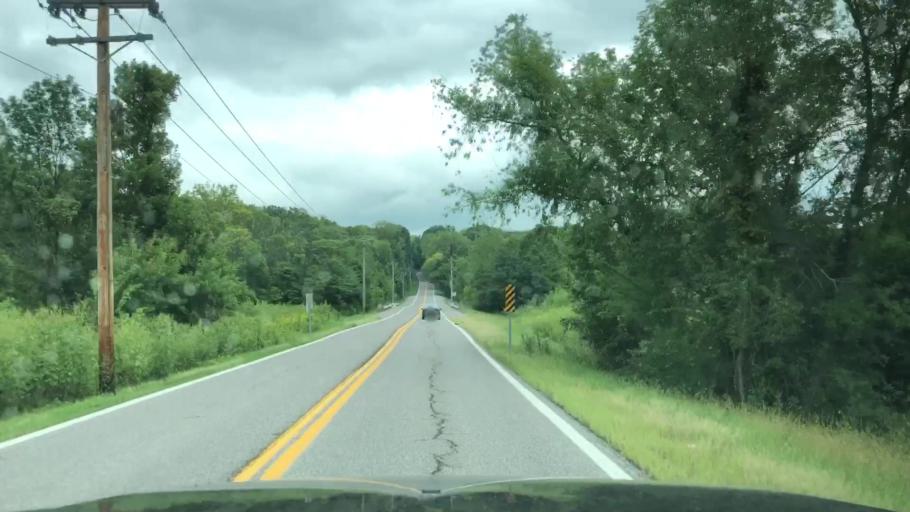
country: US
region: Missouri
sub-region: Saint Louis County
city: Hazelwood
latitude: 38.8112
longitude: -90.3934
